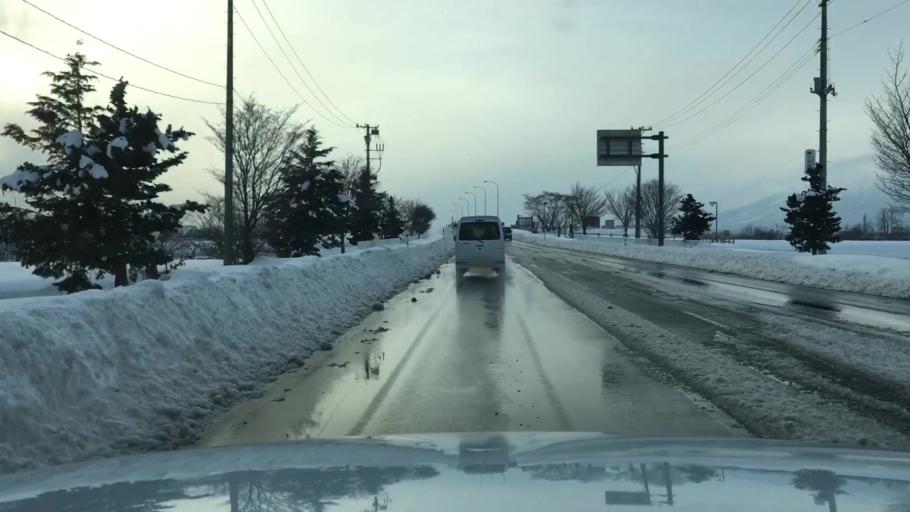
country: JP
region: Aomori
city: Hirosaki
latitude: 40.5945
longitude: 140.5307
